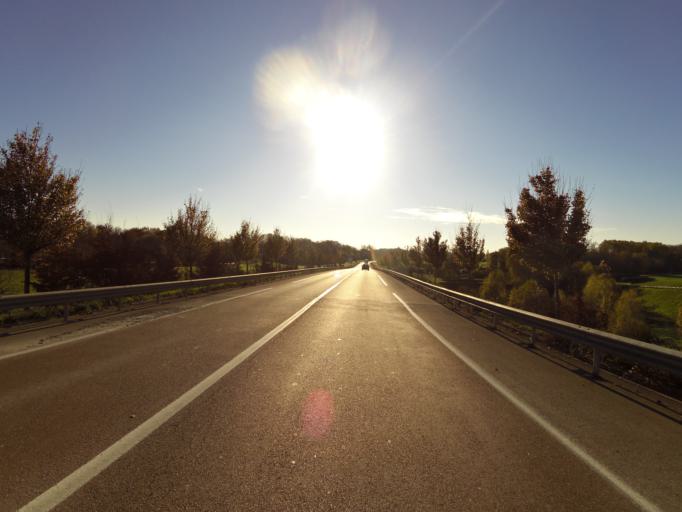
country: FR
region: Champagne-Ardenne
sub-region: Departement de l'Aube
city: Bucheres
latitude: 48.2503
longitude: 4.1125
